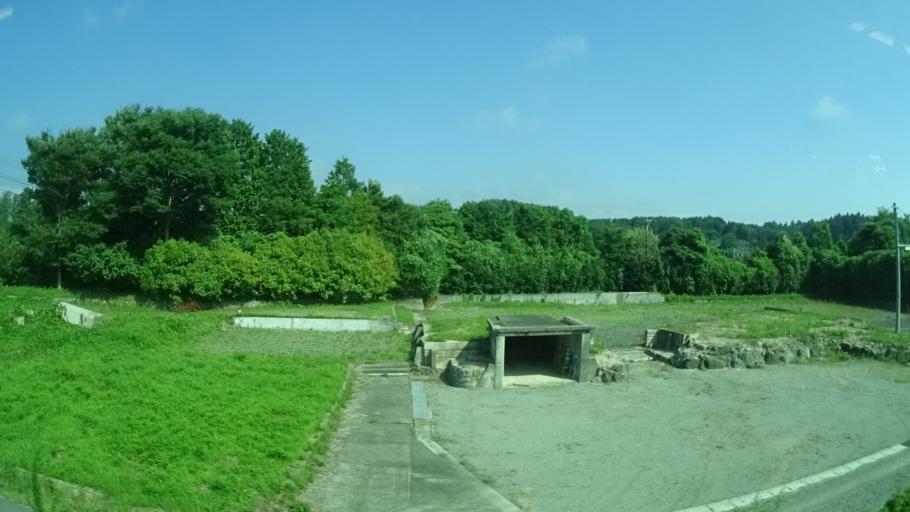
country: JP
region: Fukushima
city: Namie
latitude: 37.3195
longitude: 141.0093
